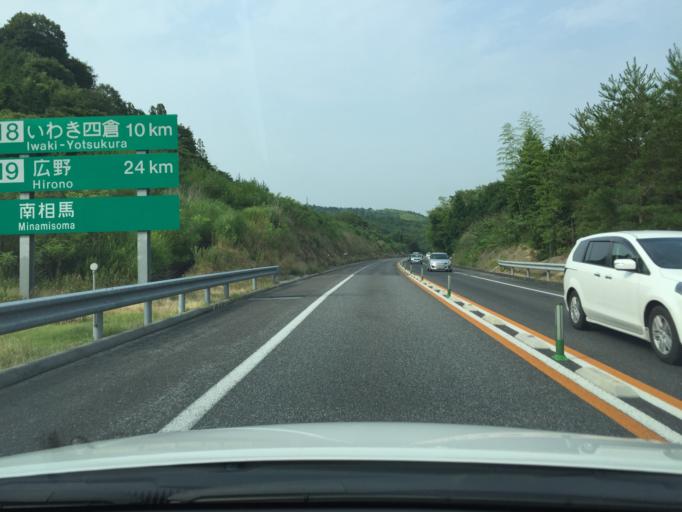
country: JP
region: Fukushima
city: Iwaki
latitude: 37.0908
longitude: 140.8438
